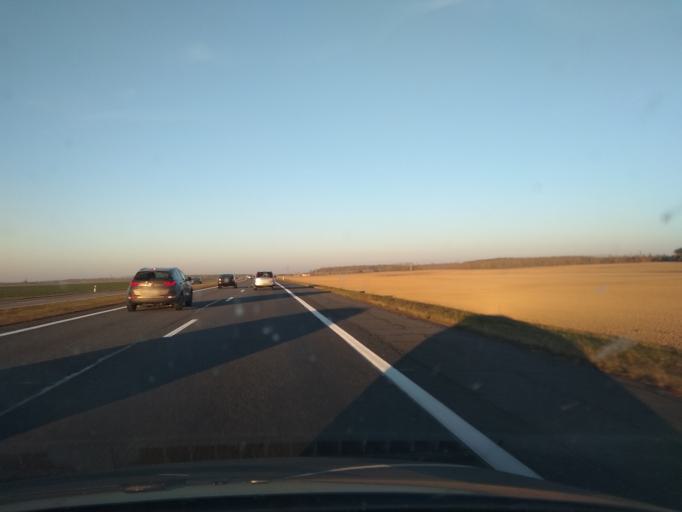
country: BY
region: Brest
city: Baranovichi
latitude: 53.2225
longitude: 26.1551
